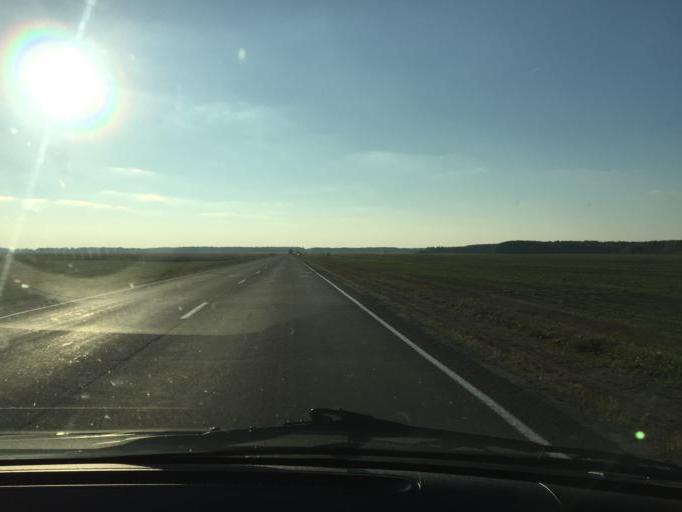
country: BY
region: Brest
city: Horad Luninyets
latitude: 52.3024
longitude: 26.4772
